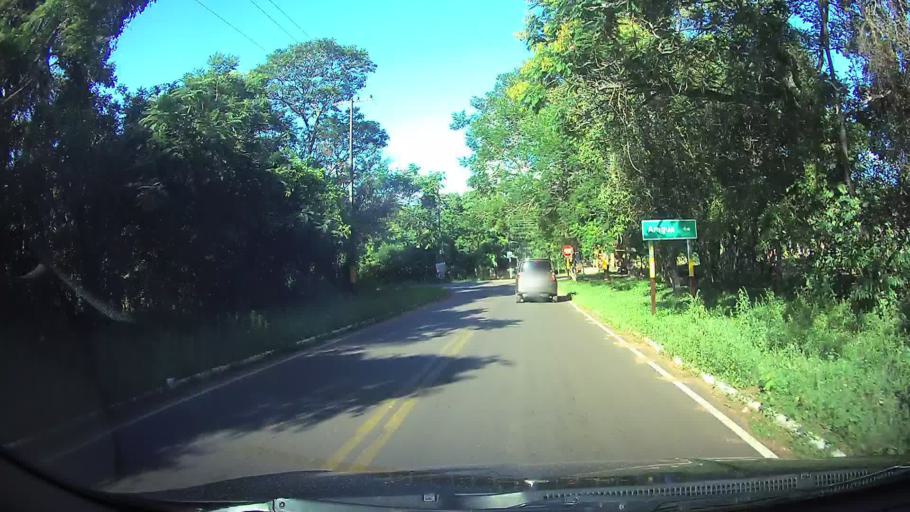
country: PY
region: Central
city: Aregua
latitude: -25.3339
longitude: -57.3820
